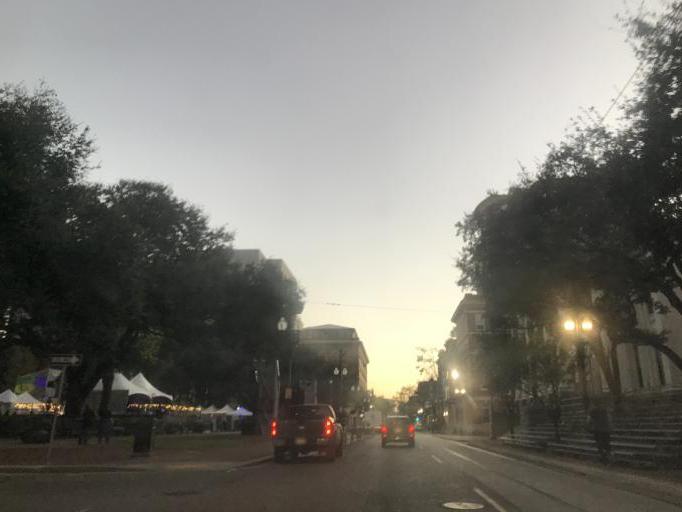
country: US
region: Louisiana
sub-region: Orleans Parish
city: New Orleans
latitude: 29.9490
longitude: -90.0707
